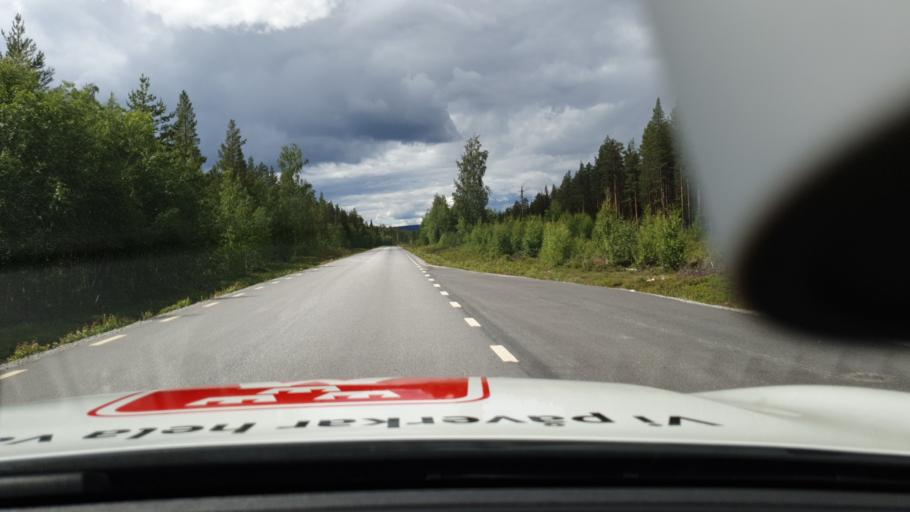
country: SE
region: Norrbotten
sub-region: Jokkmokks Kommun
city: Jokkmokk
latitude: 66.8213
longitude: 19.1733
